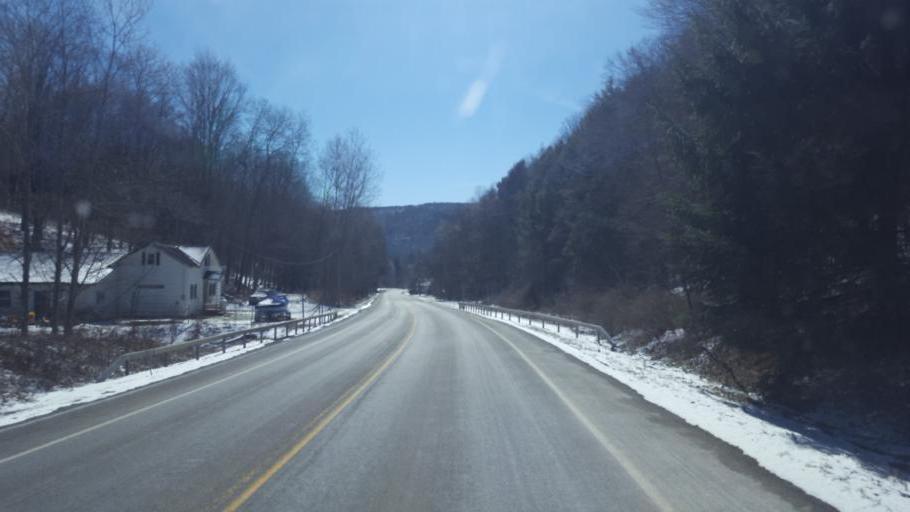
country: US
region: New York
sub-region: Allegany County
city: Andover
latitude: 42.0454
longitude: -77.7883
